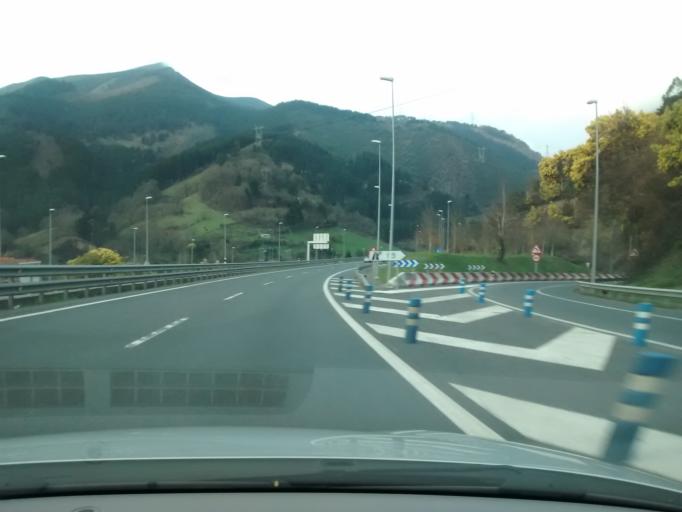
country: ES
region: Basque Country
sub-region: Bizkaia
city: Gordexola
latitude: 43.2039
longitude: -3.0430
